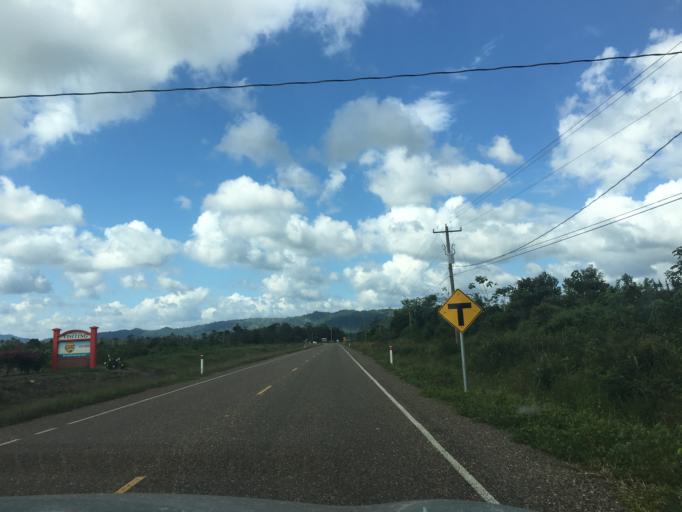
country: BZ
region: Stann Creek
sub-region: Dangriga
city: Dangriga
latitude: 16.8546
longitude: -88.3418
